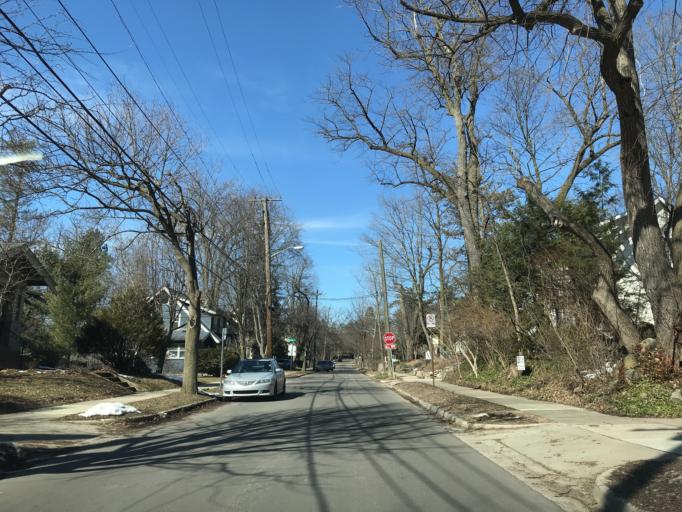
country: US
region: Michigan
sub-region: Washtenaw County
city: Ann Arbor
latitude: 42.2666
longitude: -83.7255
